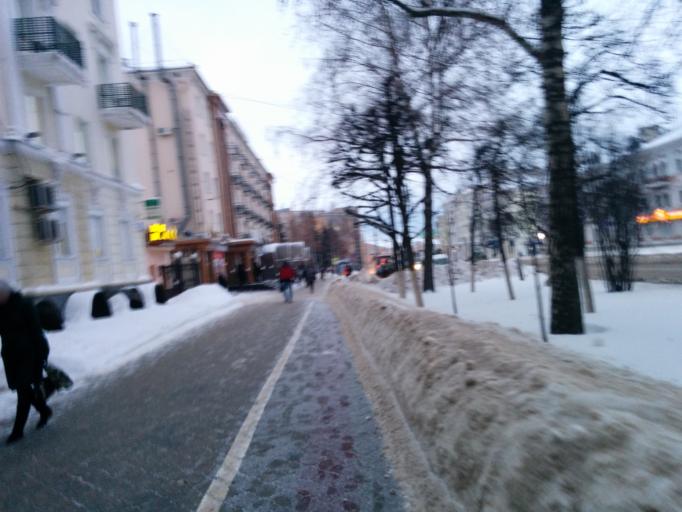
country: RU
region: Chuvashia
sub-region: Cheboksarskiy Rayon
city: Cheboksary
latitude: 56.1304
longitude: 47.2471
